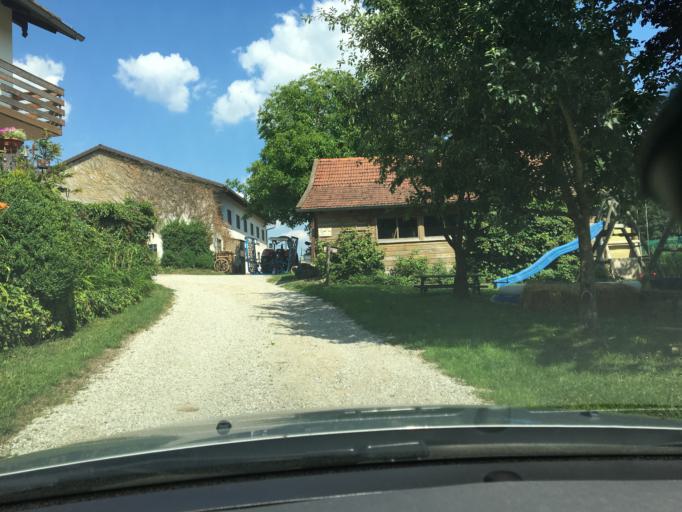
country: DE
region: Bavaria
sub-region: Upper Bavaria
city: Kirchberg
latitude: 48.4474
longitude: 12.0549
